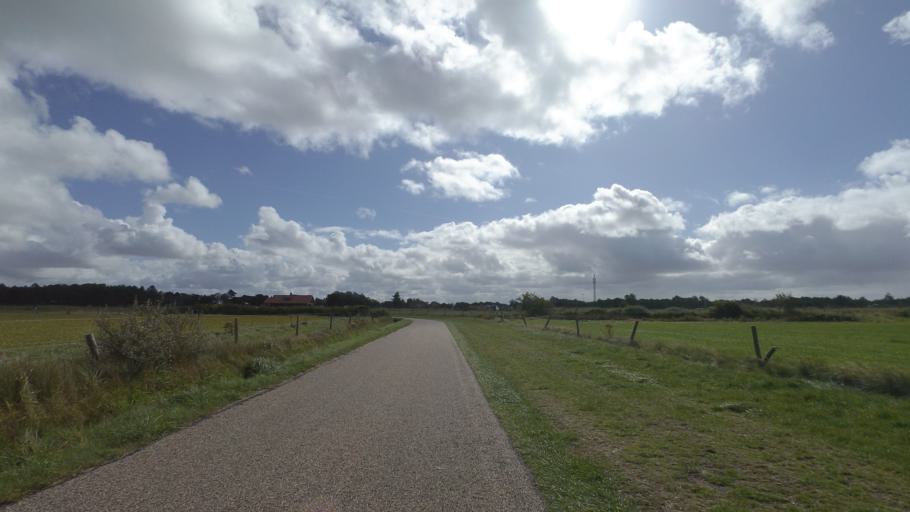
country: NL
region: Friesland
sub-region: Gemeente Ameland
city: Nes
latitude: 53.4514
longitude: 5.7925
